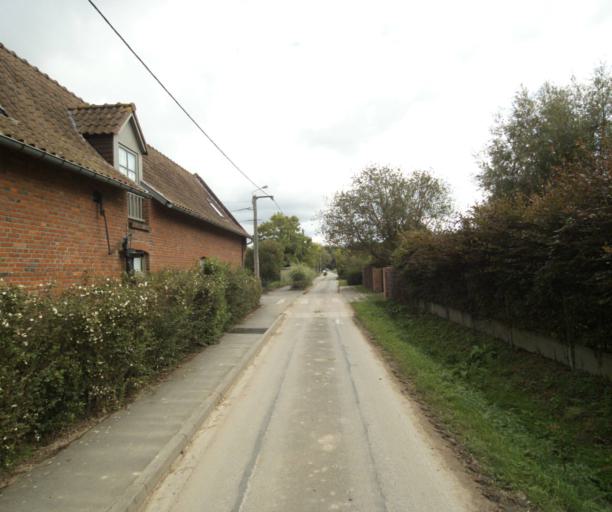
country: FR
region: Nord-Pas-de-Calais
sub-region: Departement du Nord
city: Premesques
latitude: 50.6653
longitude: 2.9493
